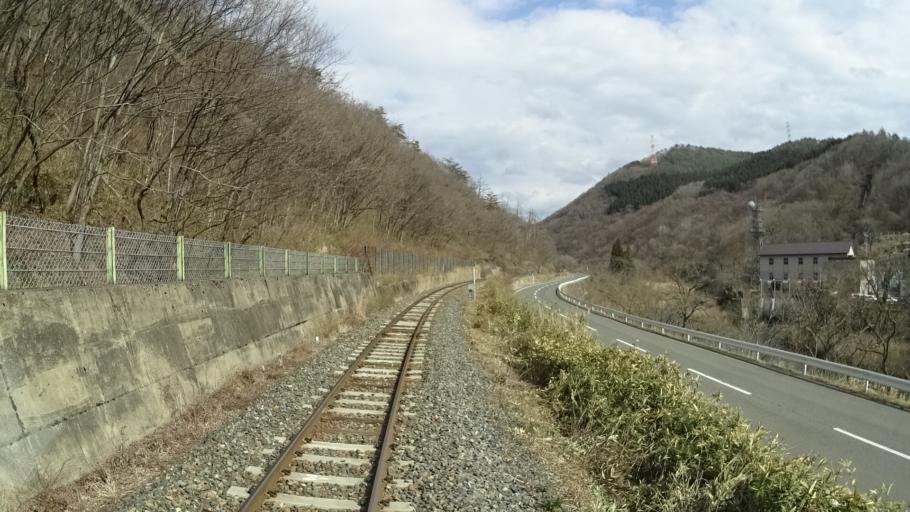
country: JP
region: Iwate
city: Hanamaki
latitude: 39.3620
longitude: 141.2857
